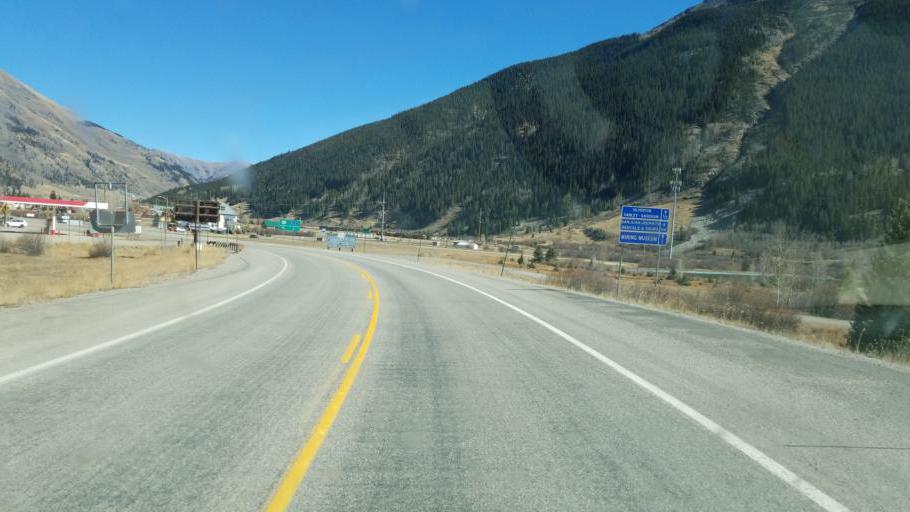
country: US
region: Colorado
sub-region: San Juan County
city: Silverton
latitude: 37.8035
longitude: -107.6727
